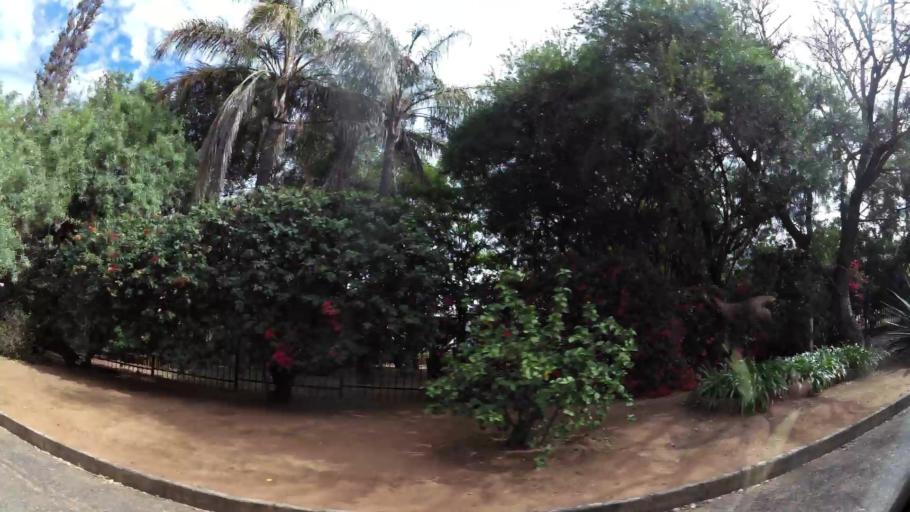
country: ZA
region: Limpopo
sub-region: Waterberg District Municipality
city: Warmbaths
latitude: -24.8866
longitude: 28.2795
